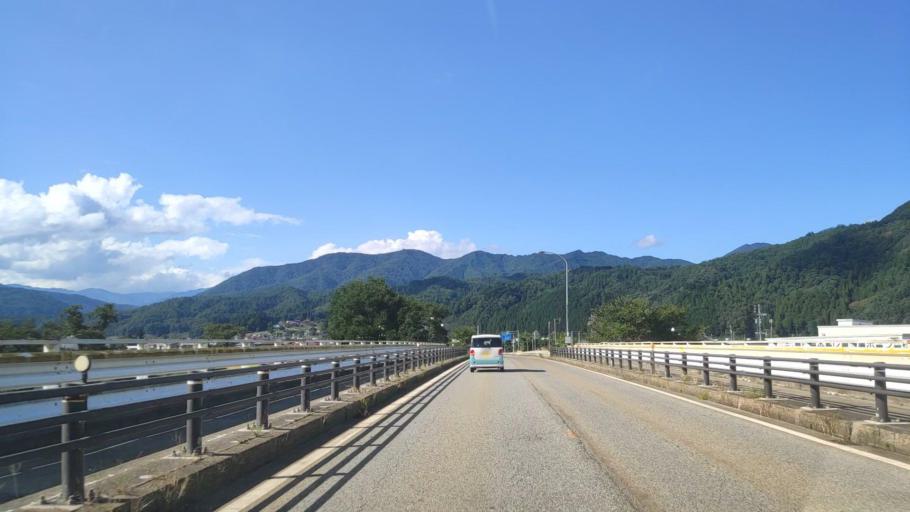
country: JP
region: Gifu
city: Takayama
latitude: 36.2493
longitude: 137.1632
